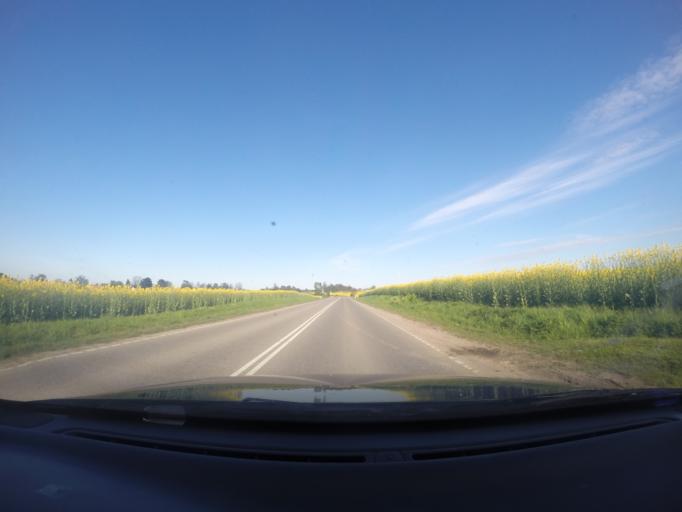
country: DK
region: Capital Region
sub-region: Hoje-Taastrup Kommune
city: Taastrup
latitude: 55.6779
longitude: 12.2535
